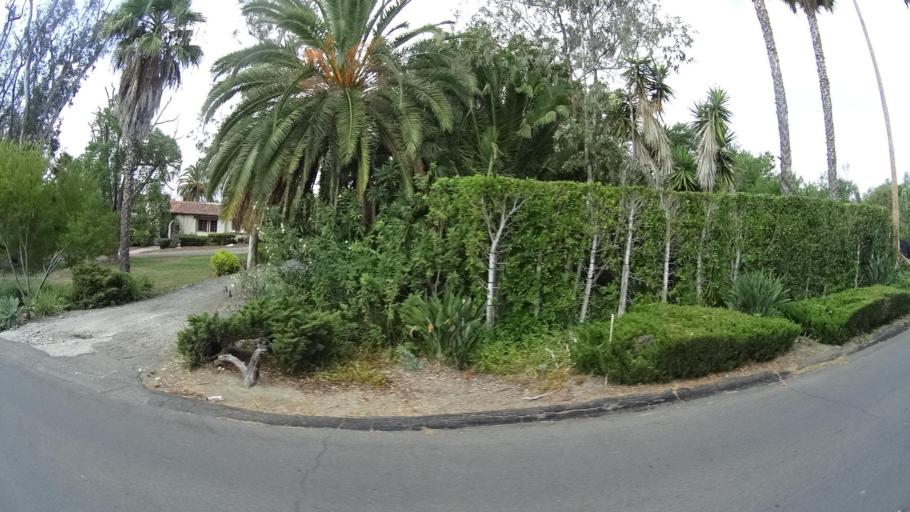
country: US
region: California
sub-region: San Diego County
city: Rancho Santa Fe
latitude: 33.0165
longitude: -117.2001
